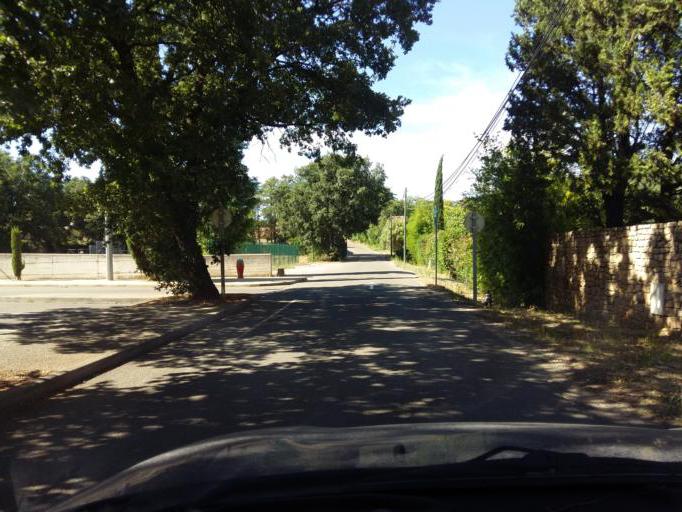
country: FR
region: Provence-Alpes-Cote d'Azur
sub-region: Departement du Vaucluse
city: Piolenc
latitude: 44.1823
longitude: 4.7591
